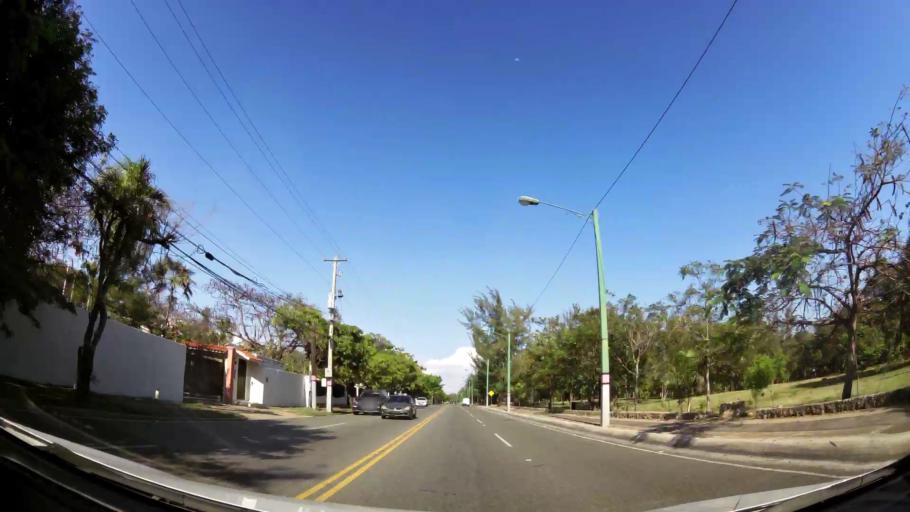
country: DO
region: Nacional
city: Bella Vista
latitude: 18.4431
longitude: -69.9574
